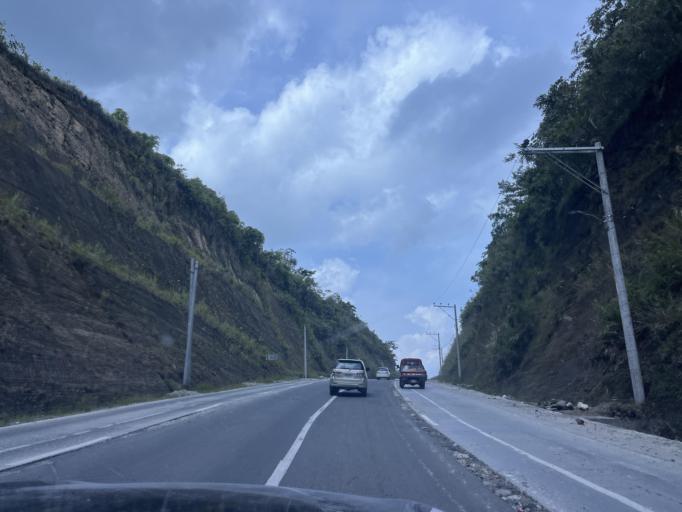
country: PH
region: Davao
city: Simod
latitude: 7.3782
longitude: 125.2784
